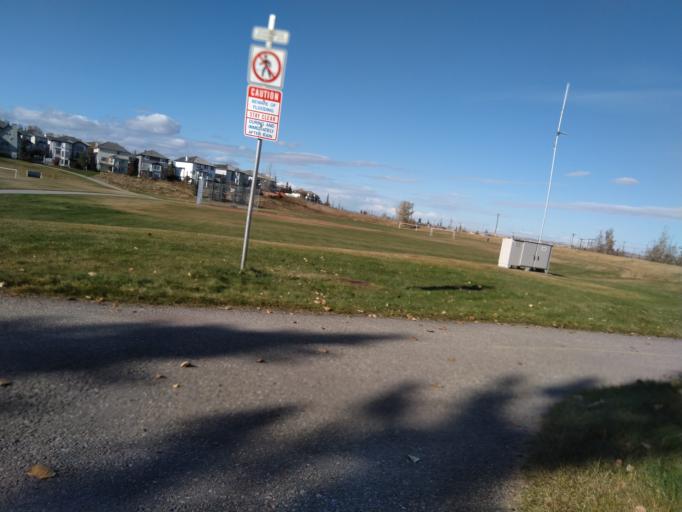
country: CA
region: Alberta
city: Calgary
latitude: 51.1398
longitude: -114.1229
